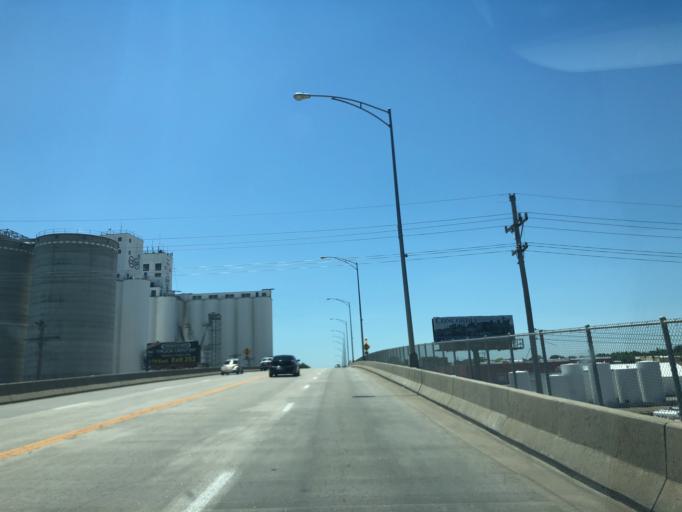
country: US
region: Kansas
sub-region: Cloud County
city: Concordia
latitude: 39.5758
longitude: -97.6576
